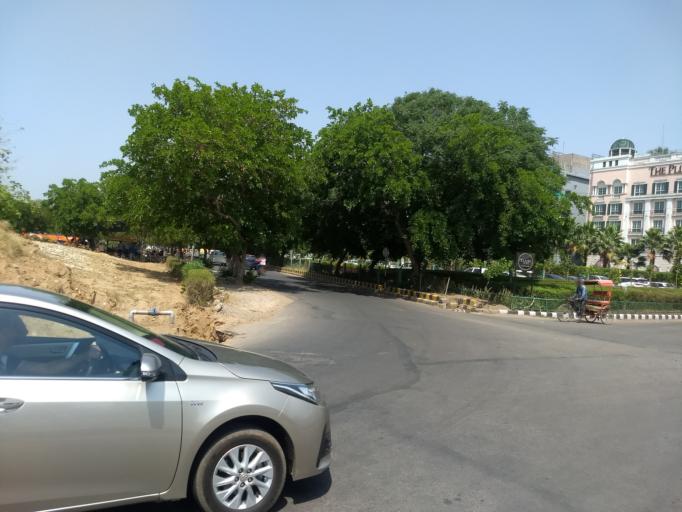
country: IN
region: Haryana
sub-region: Gurgaon
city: Gurgaon
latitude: 28.4649
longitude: 77.0631
